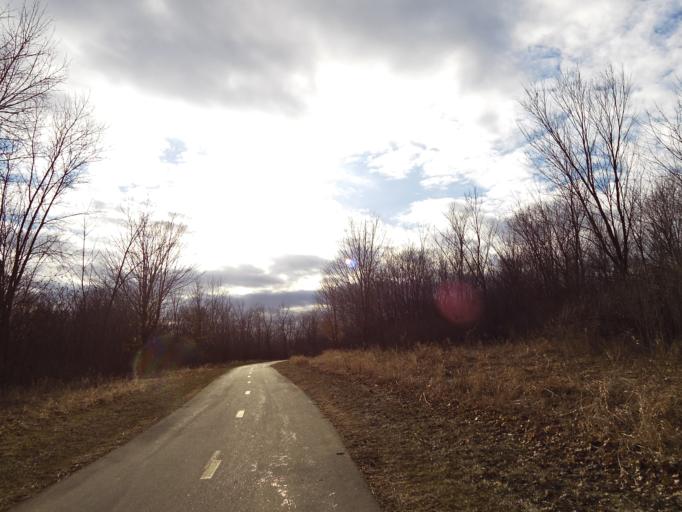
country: US
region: Minnesota
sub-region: Scott County
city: Prior Lake
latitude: 44.6954
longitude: -93.3823
